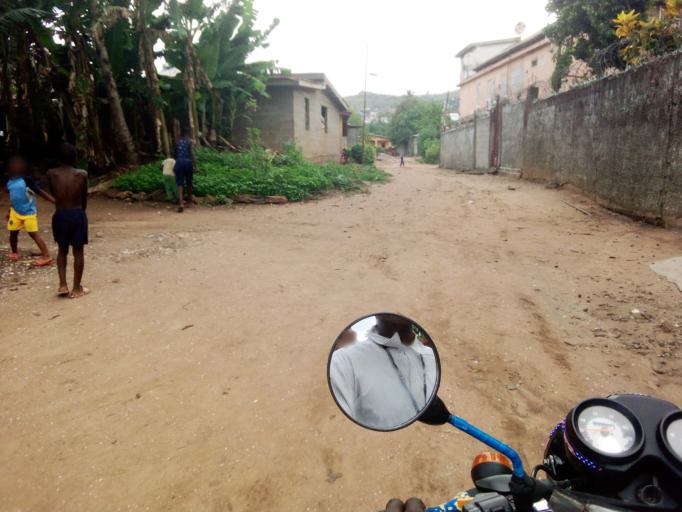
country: SL
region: Western Area
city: Waterloo
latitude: 8.3430
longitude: -13.0711
